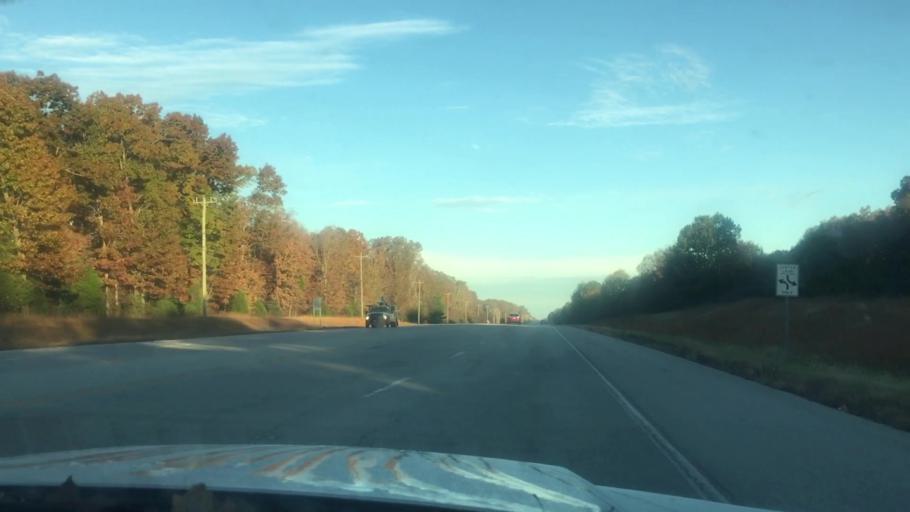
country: US
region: Tennessee
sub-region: Franklin County
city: Estill Springs
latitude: 35.3074
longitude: -86.1604
